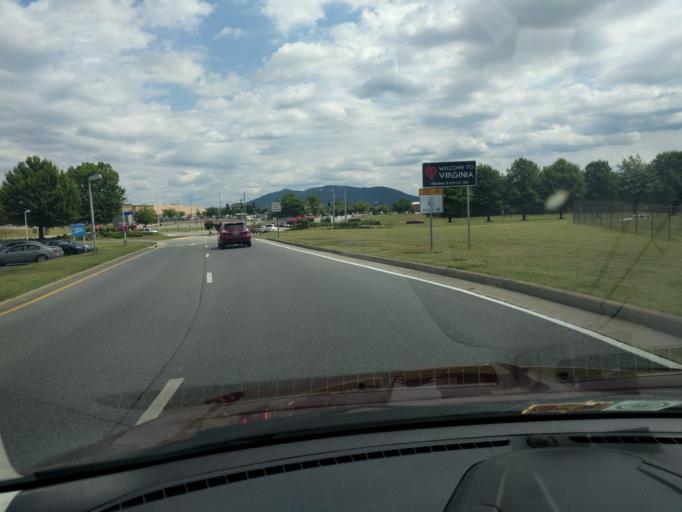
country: US
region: Virginia
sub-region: Roanoke County
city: Hollins
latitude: 37.3173
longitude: -79.9695
